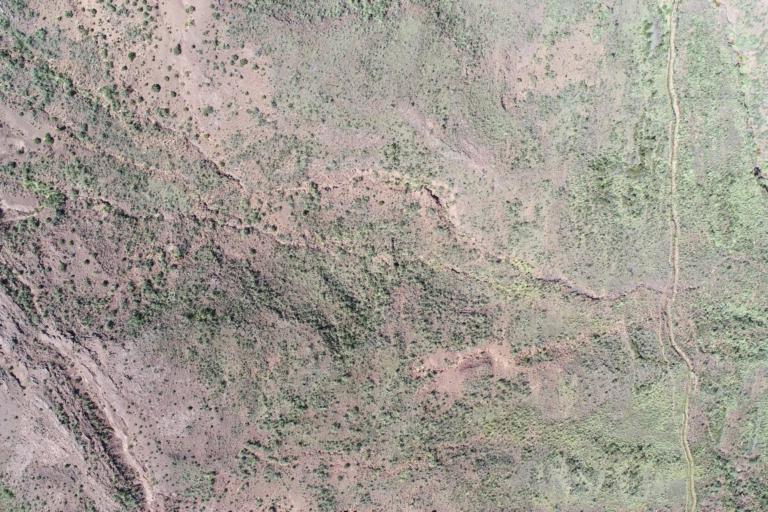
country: BO
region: La Paz
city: Tiahuanaco
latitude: -16.6048
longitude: -68.7563
